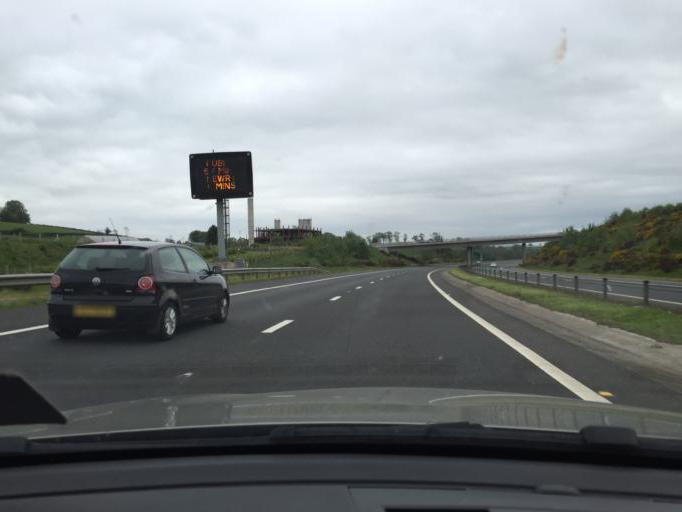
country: GB
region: Northern Ireland
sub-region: Newry and Mourne District
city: Newry
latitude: 54.2279
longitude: -6.3188
